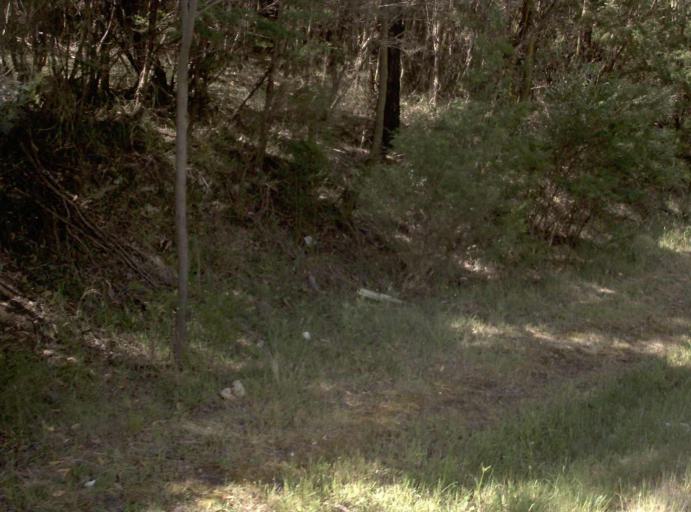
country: AU
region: Victoria
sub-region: Latrobe
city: Morwell
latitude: -38.1561
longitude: 146.4301
